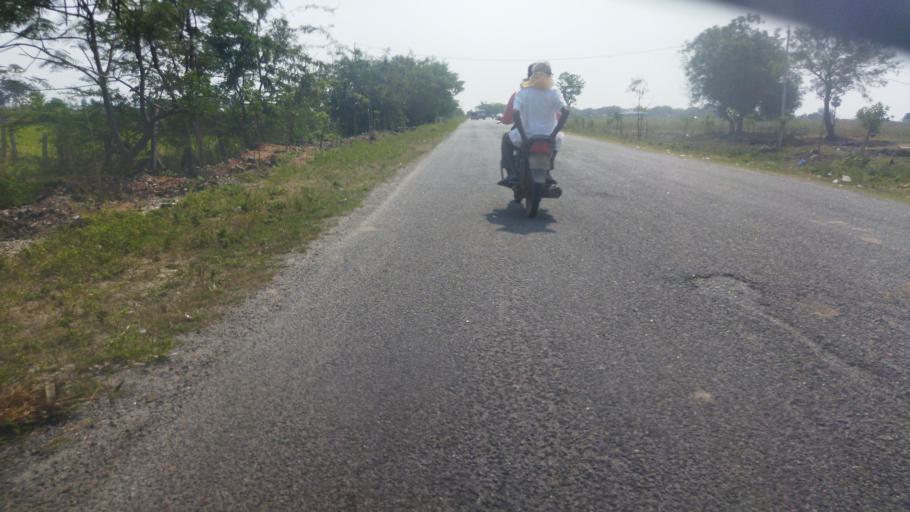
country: IN
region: Telangana
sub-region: Nalgonda
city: Nalgonda
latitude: 17.1003
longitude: 79.2845
